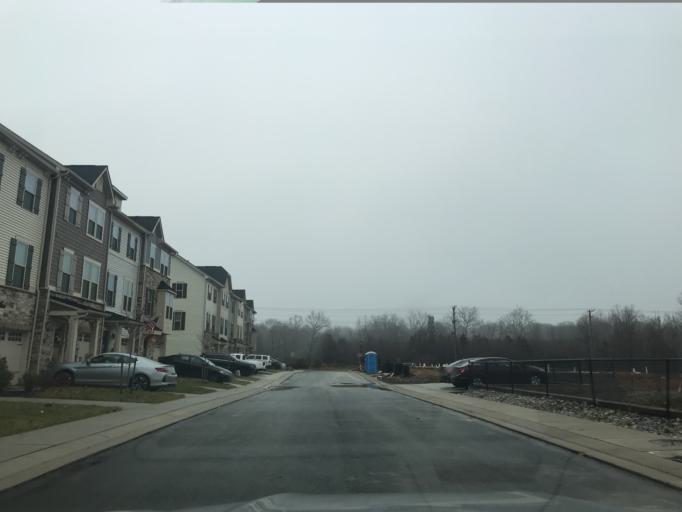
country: US
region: Maryland
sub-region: Harford County
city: South Bel Air
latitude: 39.5458
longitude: -76.3307
